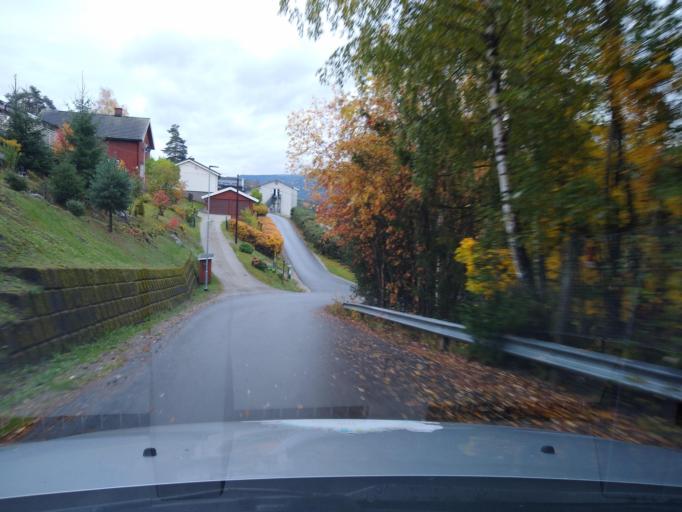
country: NO
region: Oppland
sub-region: Ringebu
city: Ringebu
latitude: 61.4573
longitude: 10.1989
